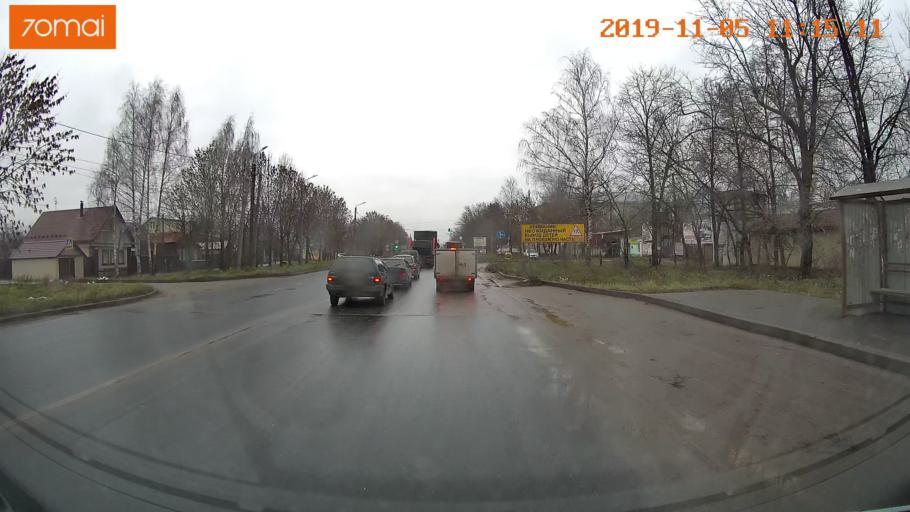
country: RU
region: Ivanovo
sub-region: Gorod Ivanovo
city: Ivanovo
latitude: 56.9768
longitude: 40.9542
